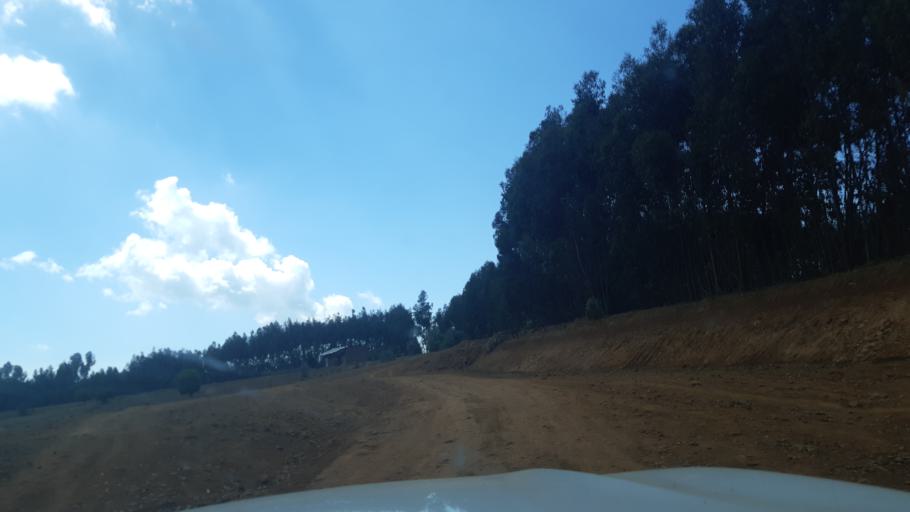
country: ET
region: Amhara
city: Dabat
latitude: 13.3621
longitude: 37.3843
